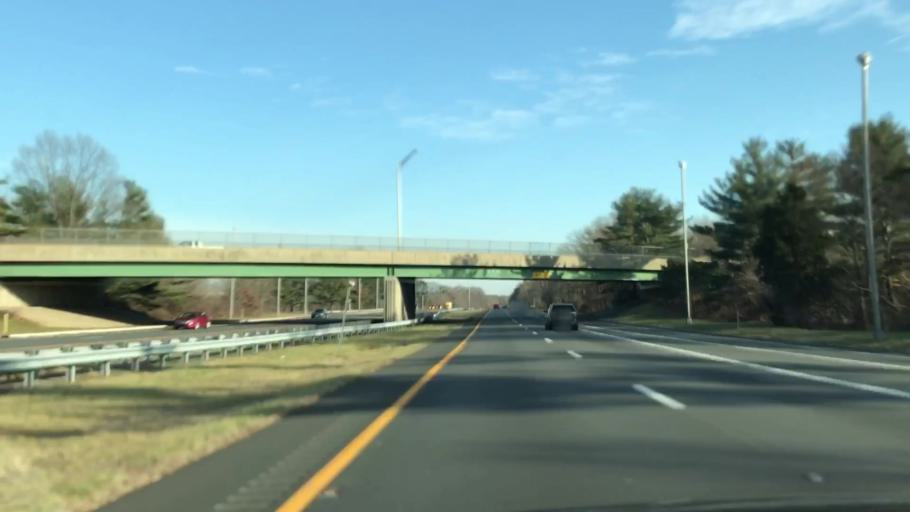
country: US
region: New Jersey
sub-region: Monmouth County
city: Allentown
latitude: 40.1918
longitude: -74.5935
